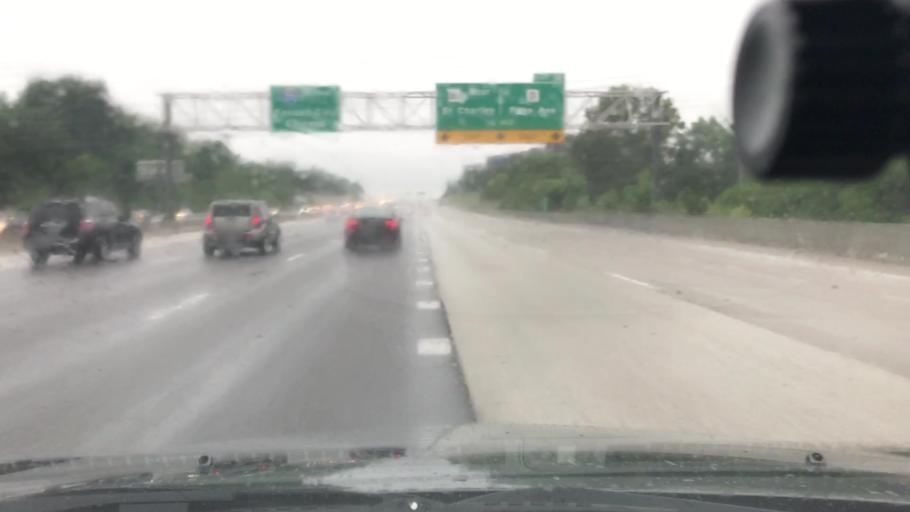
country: US
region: Missouri
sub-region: Saint Louis County
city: Maryland Heights
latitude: 38.6858
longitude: -90.4498
